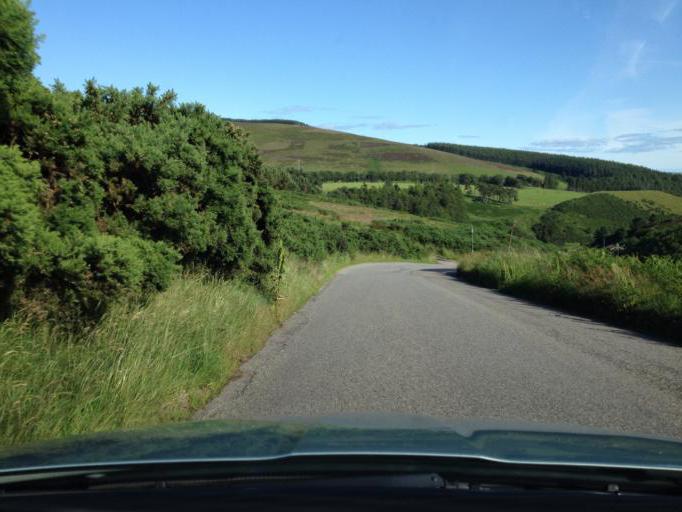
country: GB
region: Scotland
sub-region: Aberdeenshire
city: Laurencekirk
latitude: 56.8972
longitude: -2.5563
